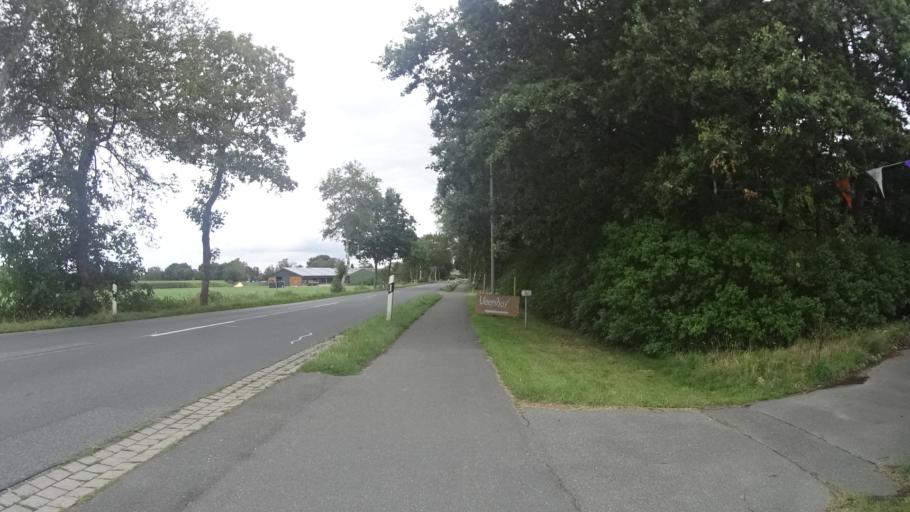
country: DE
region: Lower Saxony
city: Schiffdorf
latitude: 53.5463
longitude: 8.6850
